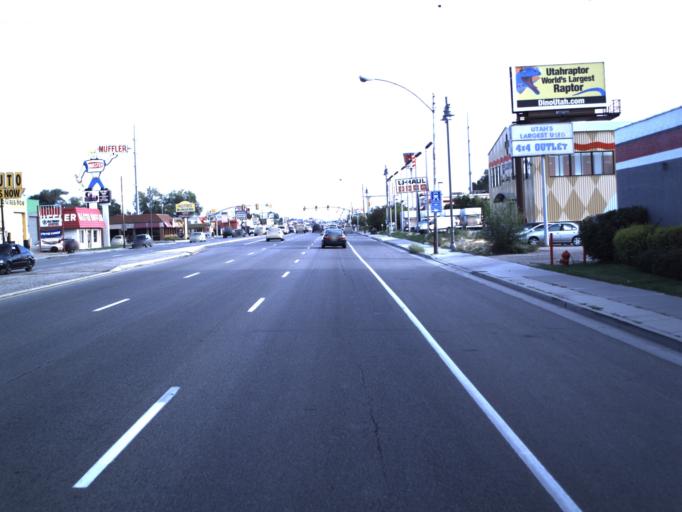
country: US
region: Utah
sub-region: Salt Lake County
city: Centerfield
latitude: 40.6890
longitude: -111.8884
